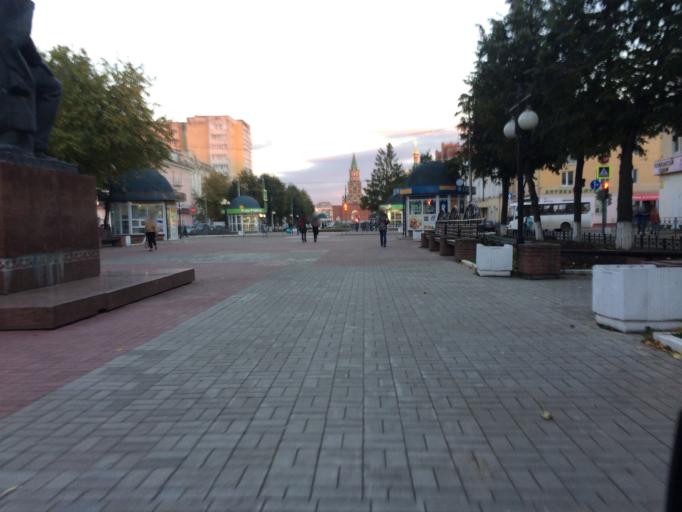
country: RU
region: Mariy-El
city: Yoshkar-Ola
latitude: 56.6350
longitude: 47.8965
